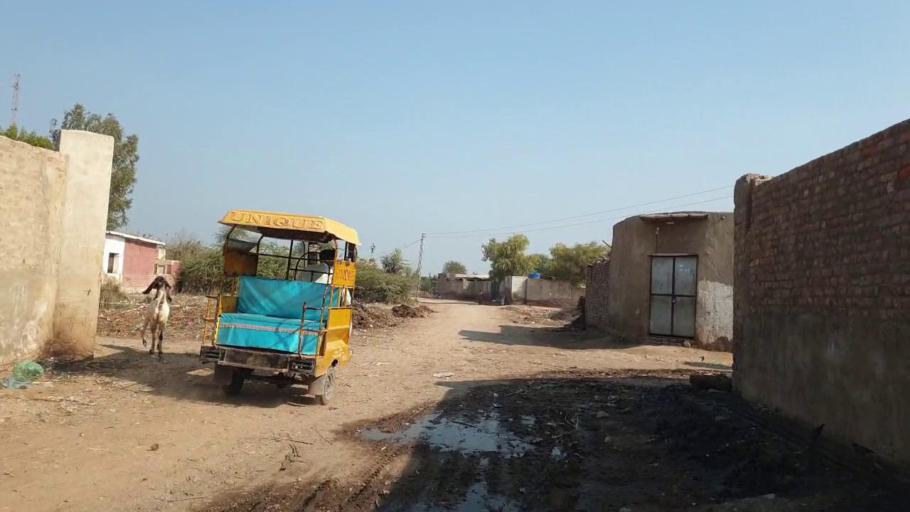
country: PK
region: Sindh
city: Tando Adam
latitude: 25.6762
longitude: 68.5655
